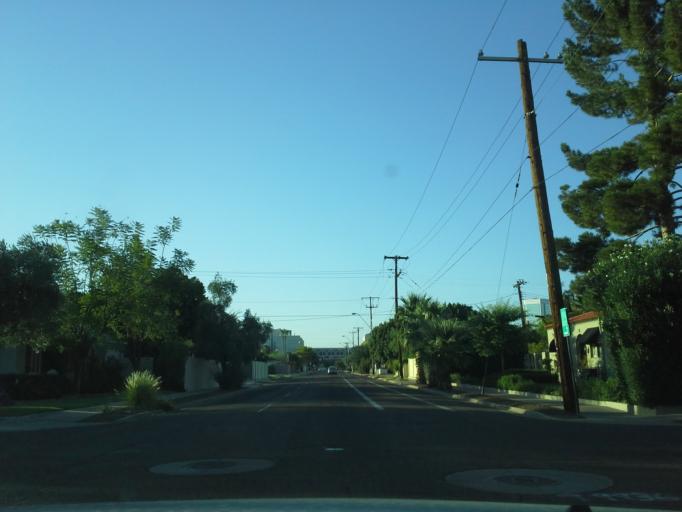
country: US
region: Arizona
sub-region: Maricopa County
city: Phoenix
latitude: 33.4766
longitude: -112.0782
